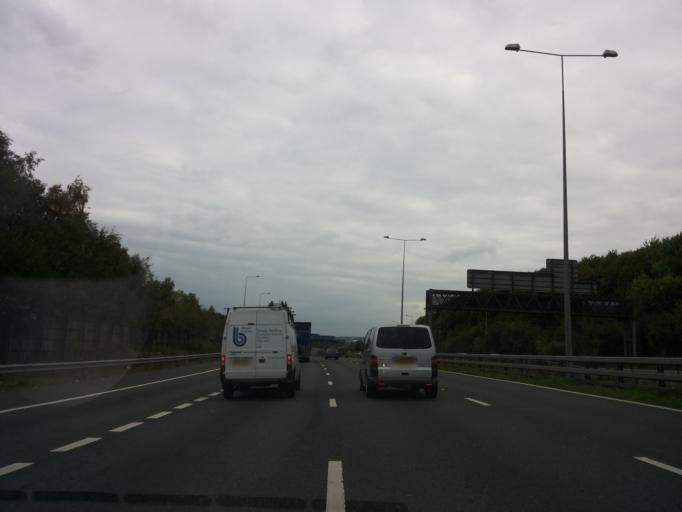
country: GB
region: England
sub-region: Medway
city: Cuxton
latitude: 51.3932
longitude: 0.4575
